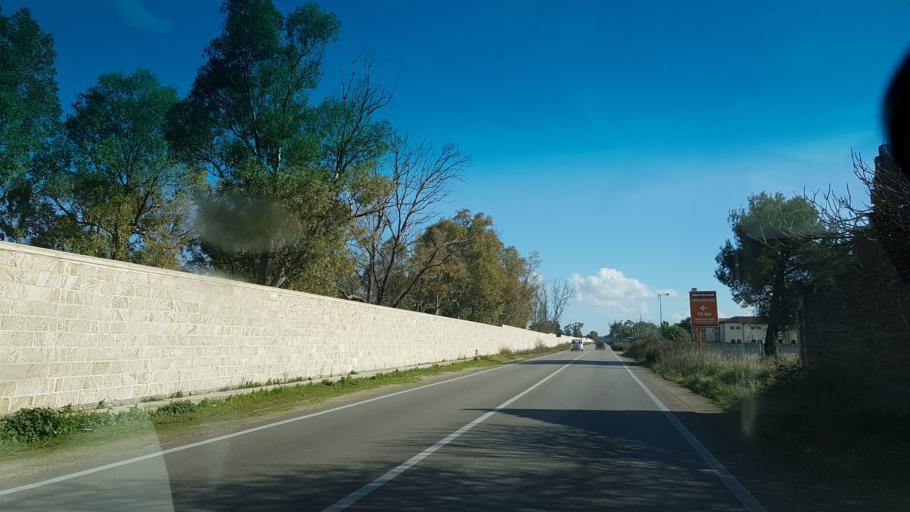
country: IT
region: Apulia
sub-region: Provincia di Lecce
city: Arnesano
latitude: 40.3589
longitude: 18.1135
